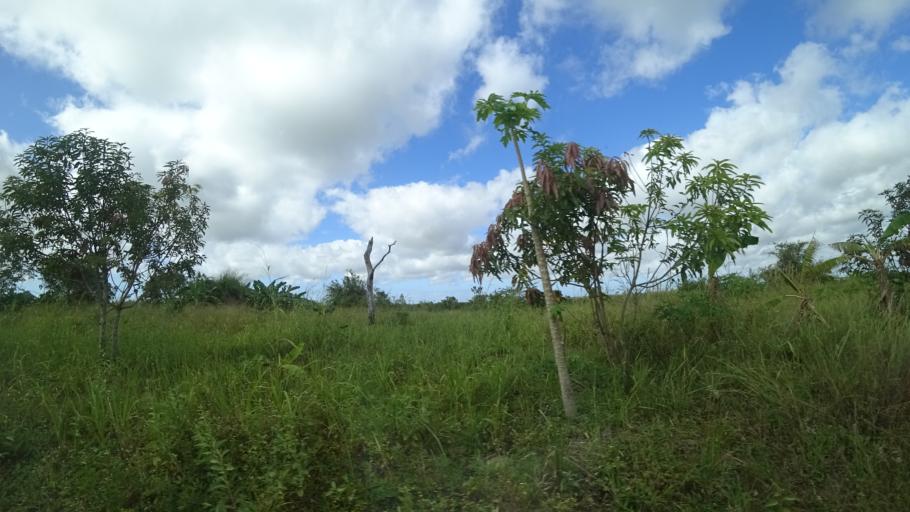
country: MZ
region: Sofala
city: Dondo
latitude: -19.5755
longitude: 35.0944
